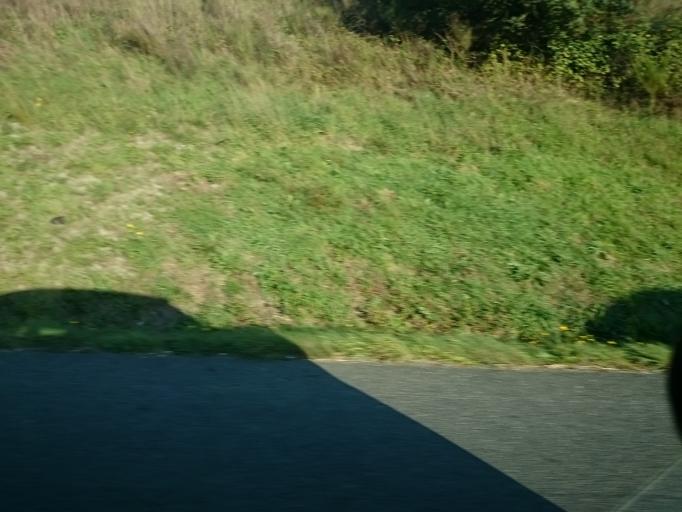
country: FR
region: Brittany
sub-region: Departement d'Ille-et-Vilaine
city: Pance
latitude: 47.8773
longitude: -1.6891
